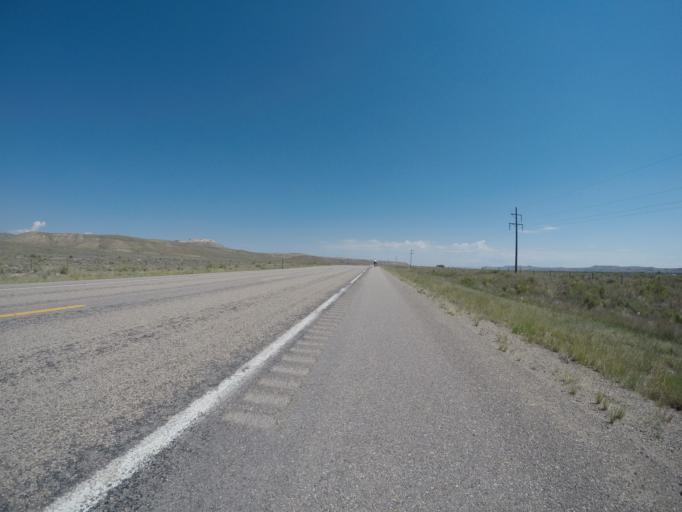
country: US
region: Wyoming
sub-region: Sublette County
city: Marbleton
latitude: 42.3621
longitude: -110.1537
